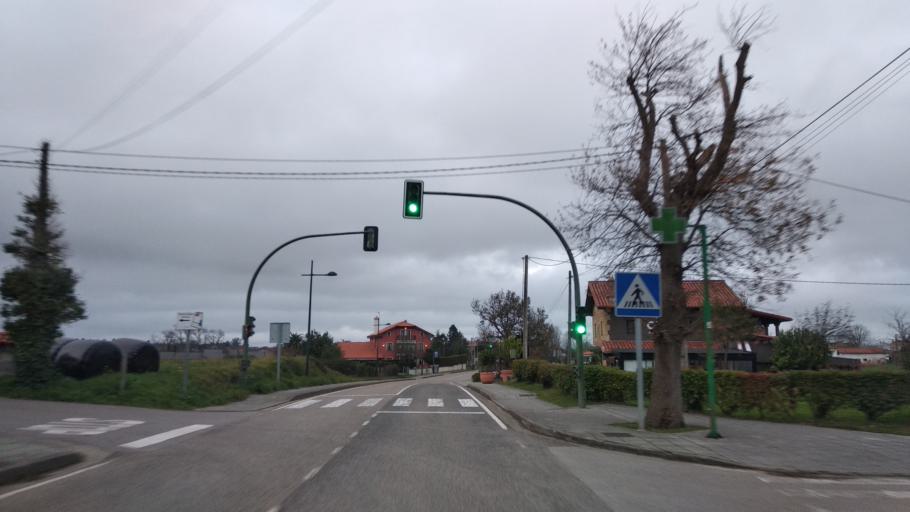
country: ES
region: Cantabria
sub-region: Provincia de Cantabria
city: Entrambasaguas
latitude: 43.4404
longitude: -3.7154
